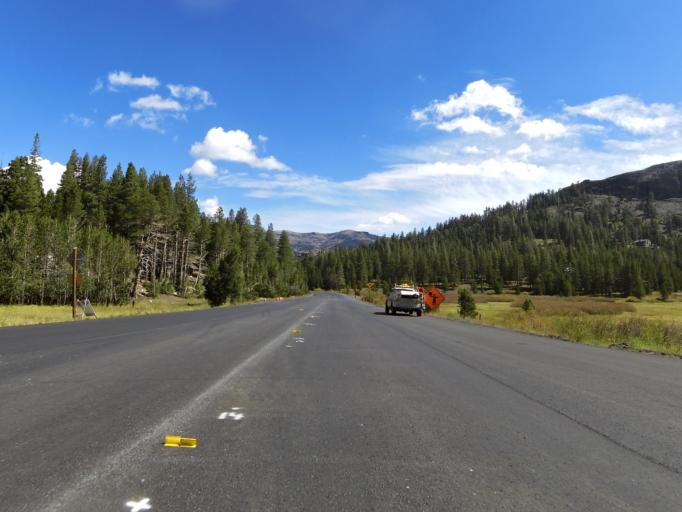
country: US
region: California
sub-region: El Dorado County
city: South Lake Tahoe
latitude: 38.7008
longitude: -120.0770
